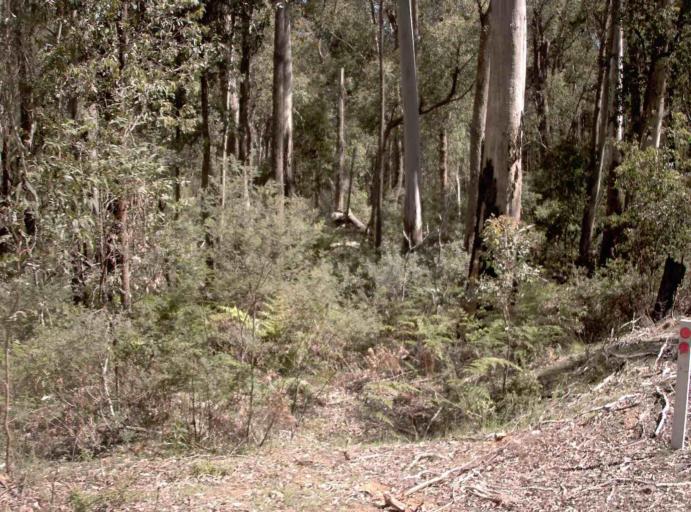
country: AU
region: New South Wales
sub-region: Bombala
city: Bombala
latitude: -37.1297
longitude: 148.7461
